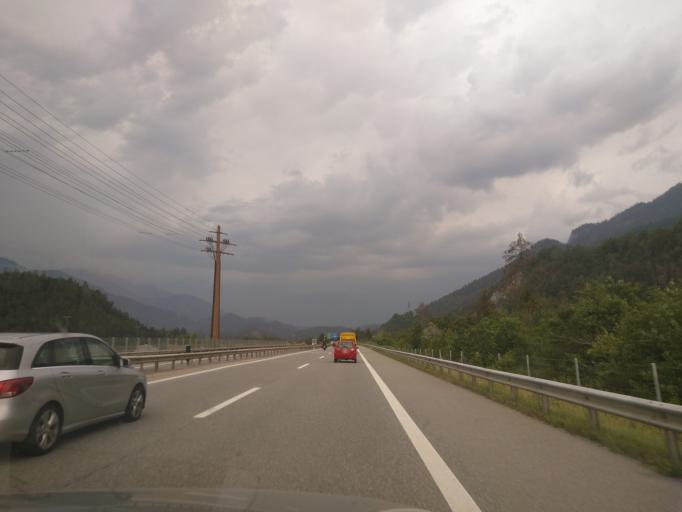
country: CH
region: Grisons
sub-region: Imboden District
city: Tamins
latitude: 46.8315
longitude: 9.4266
